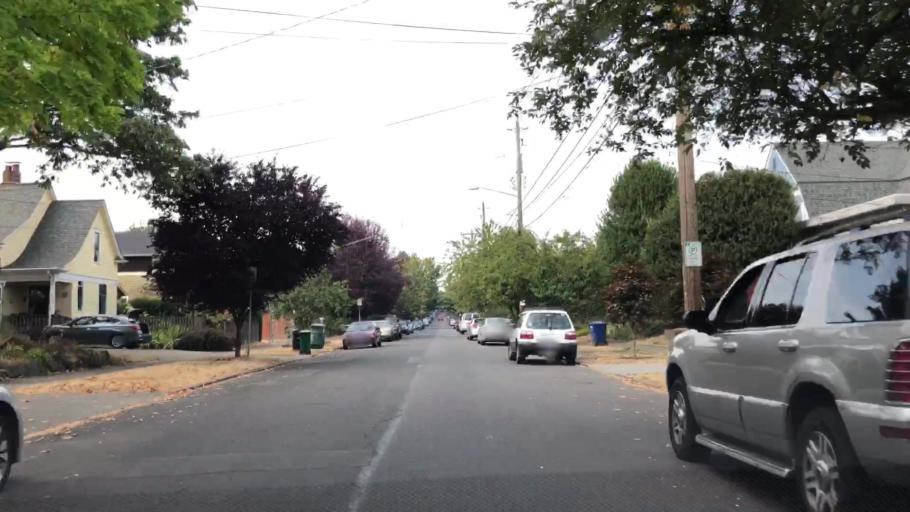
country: US
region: Washington
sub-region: King County
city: Seattle
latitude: 47.6045
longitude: -122.3076
